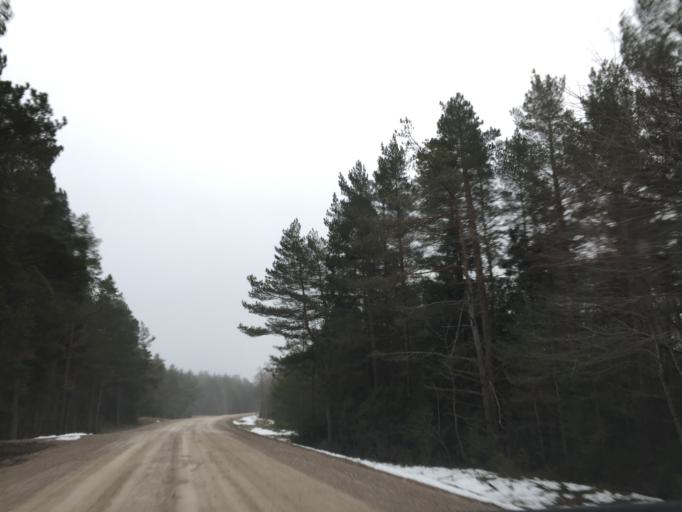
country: EE
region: Saare
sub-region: Kuressaare linn
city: Kuressaare
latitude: 58.4851
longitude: 21.9956
